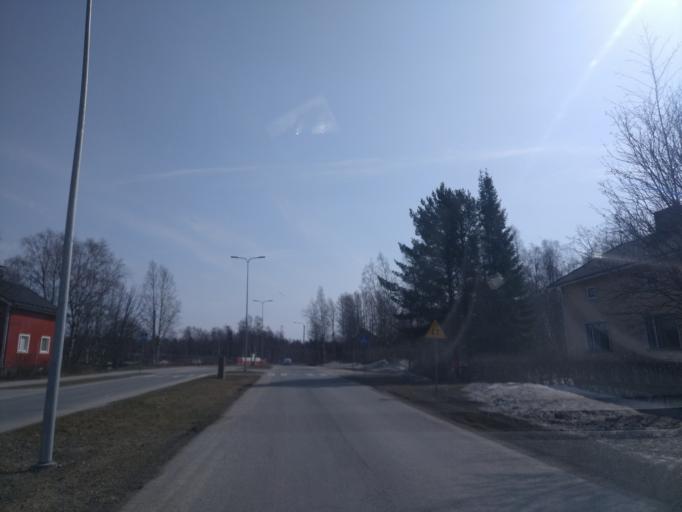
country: FI
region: Lapland
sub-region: Kemi-Tornio
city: Kemi
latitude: 65.7281
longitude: 24.6115
